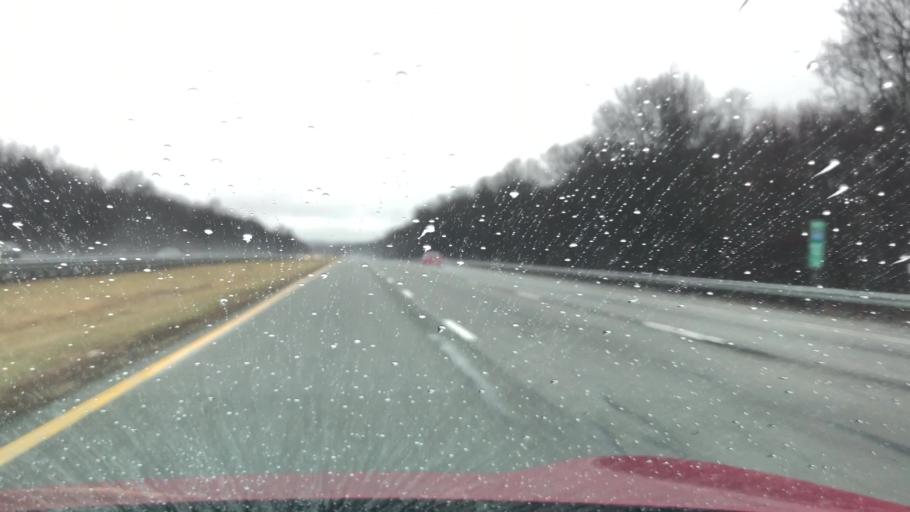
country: US
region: New Jersey
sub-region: Essex County
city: Fairfield
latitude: 40.8939
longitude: -74.2883
